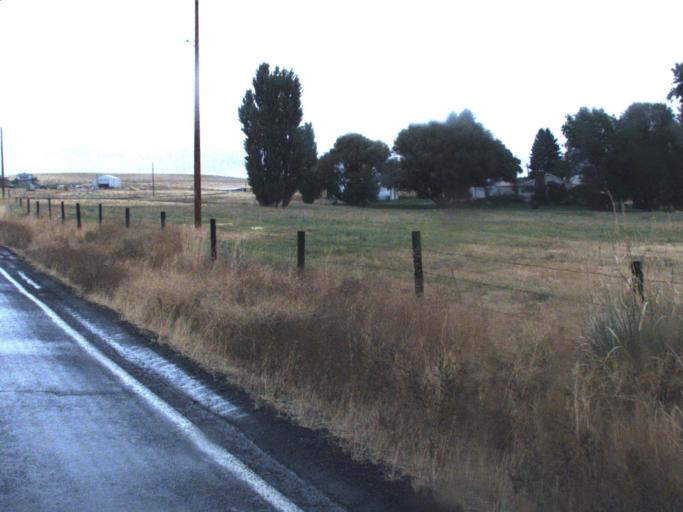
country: US
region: Washington
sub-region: Lincoln County
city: Davenport
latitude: 47.3369
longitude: -118.0028
